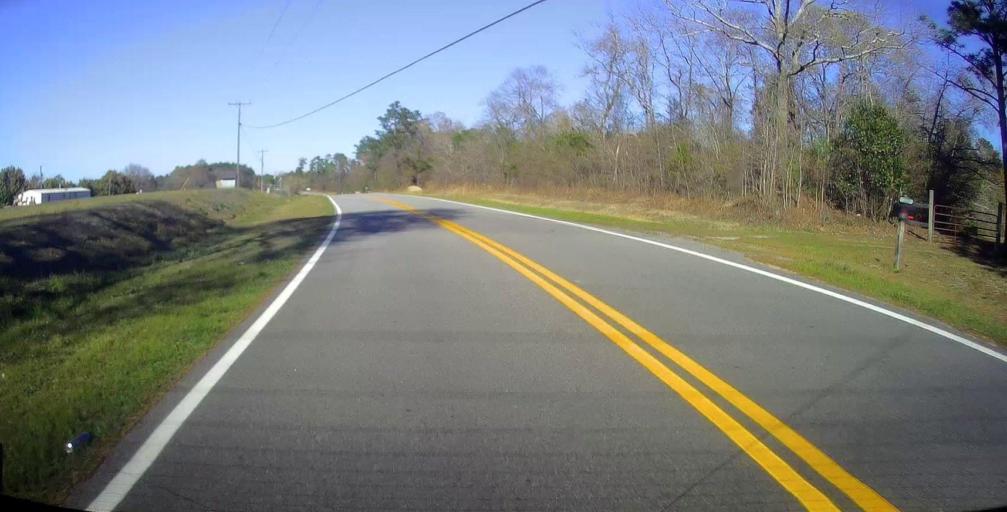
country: US
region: Georgia
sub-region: Peach County
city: Byron
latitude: 32.6767
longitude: -83.8106
